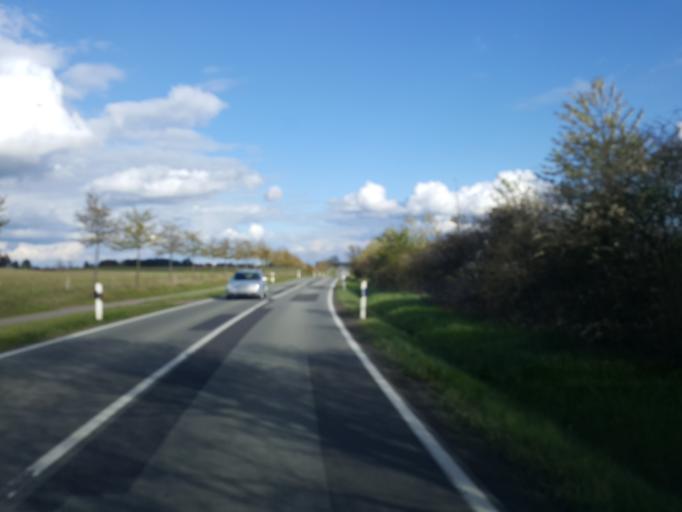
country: DE
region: Mecklenburg-Vorpommern
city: Grabowhofe
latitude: 53.5325
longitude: 12.6265
